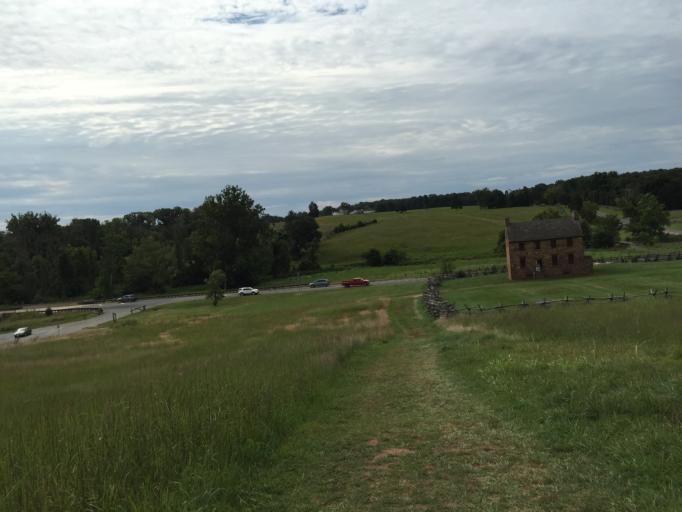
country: US
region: Virginia
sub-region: Prince William County
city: Bull Run
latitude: 38.8198
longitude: -77.5263
